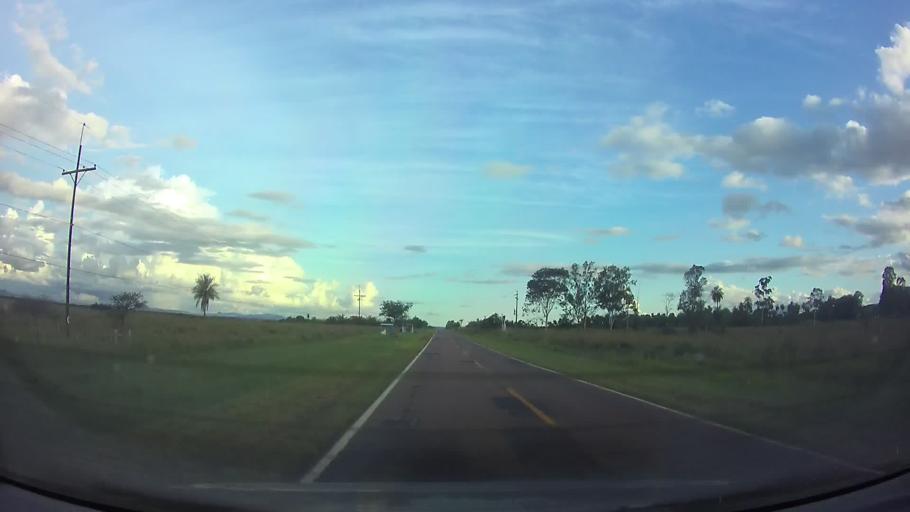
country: PY
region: Paraguari
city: Carapegua
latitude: -25.8148
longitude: -57.1758
